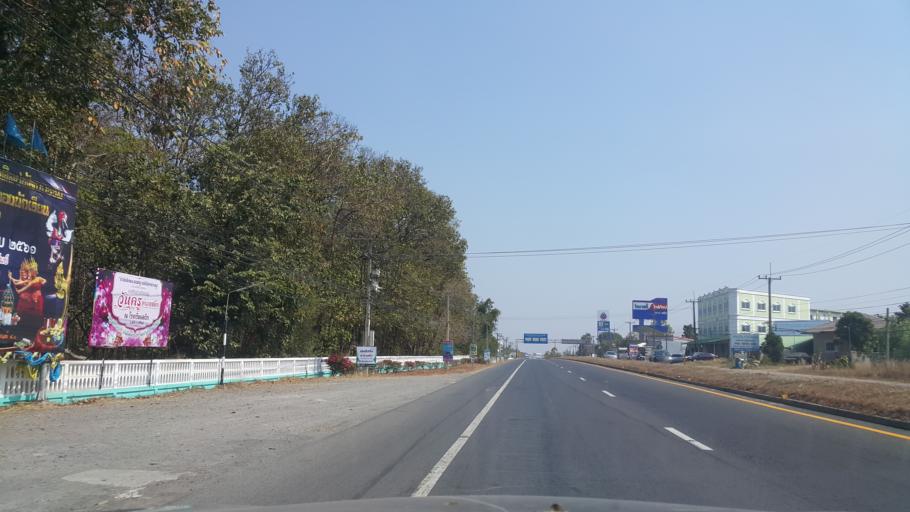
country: TH
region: Buriram
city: Satuek
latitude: 15.2772
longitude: 103.2765
